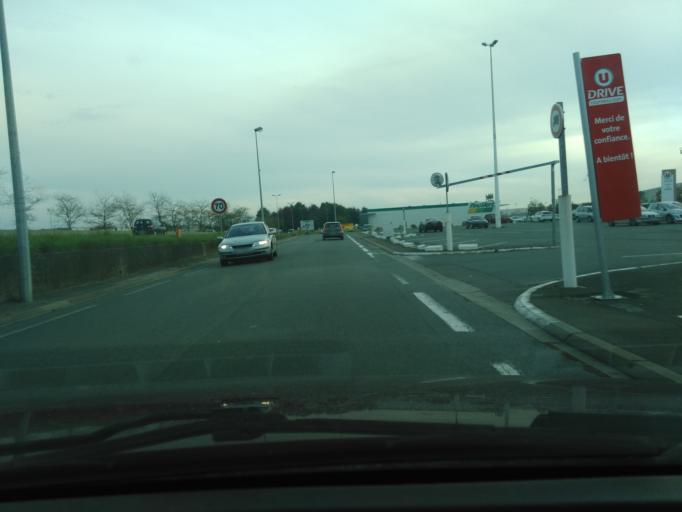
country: FR
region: Pays de la Loire
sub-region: Departement de la Vendee
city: Mouilleron-le-Captif
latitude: 46.7018
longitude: -1.4300
